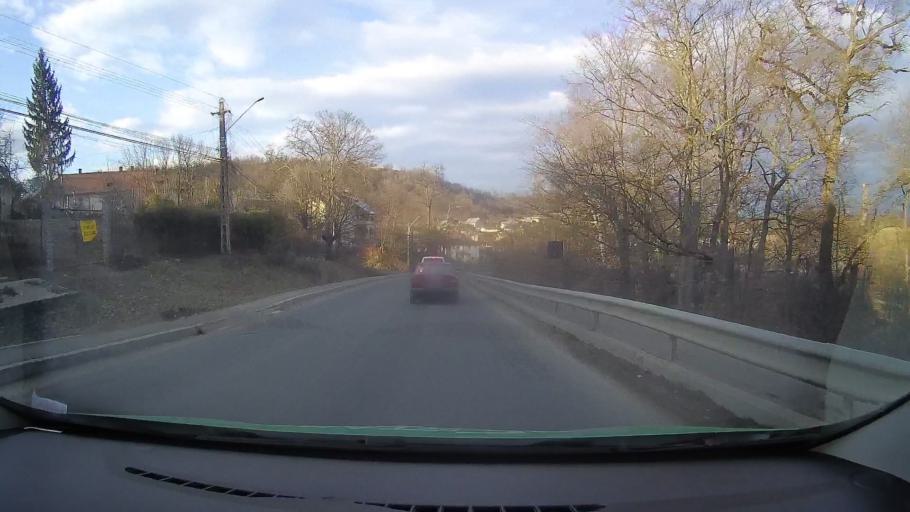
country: RO
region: Dambovita
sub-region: Municipiul Moreni
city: Moreni
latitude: 44.9757
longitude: 25.6194
